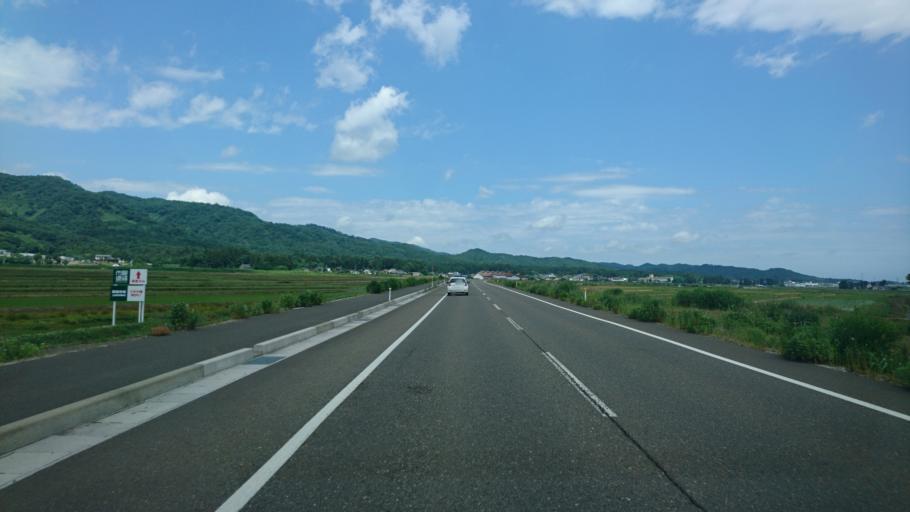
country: JP
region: Niigata
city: Arai
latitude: 37.0712
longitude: 138.2374
